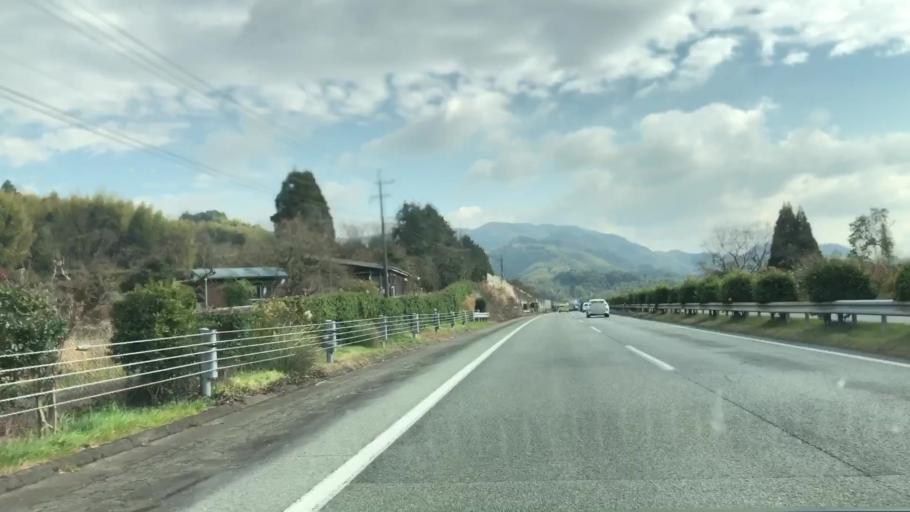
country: JP
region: Fukuoka
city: Setakamachi-takayanagi
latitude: 33.1178
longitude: 130.5255
